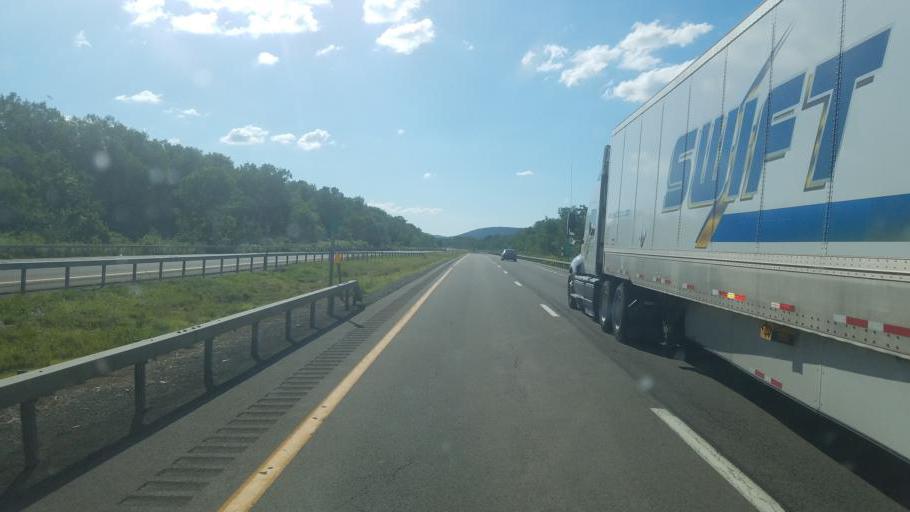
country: US
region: New York
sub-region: Cattaraugus County
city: Randolph
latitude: 42.1008
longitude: -78.8629
